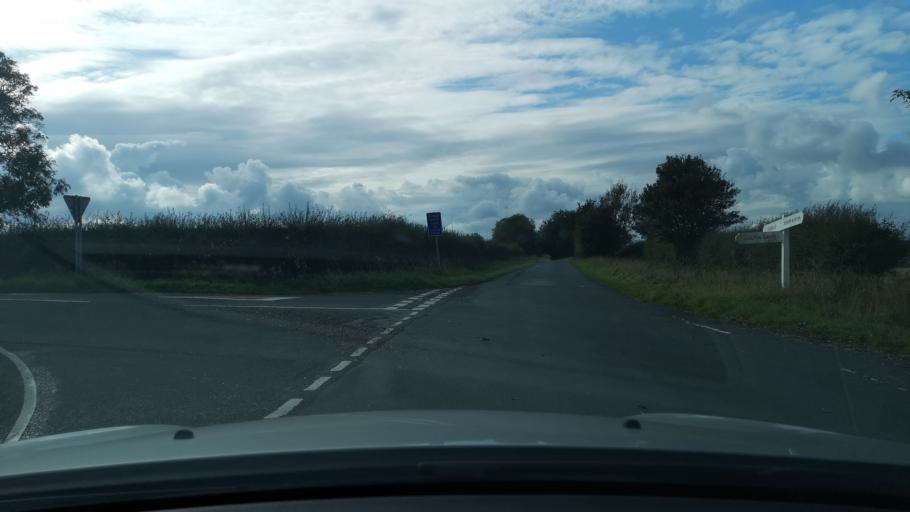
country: GB
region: England
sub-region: East Riding of Yorkshire
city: Walkington
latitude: 53.8255
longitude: -0.5255
